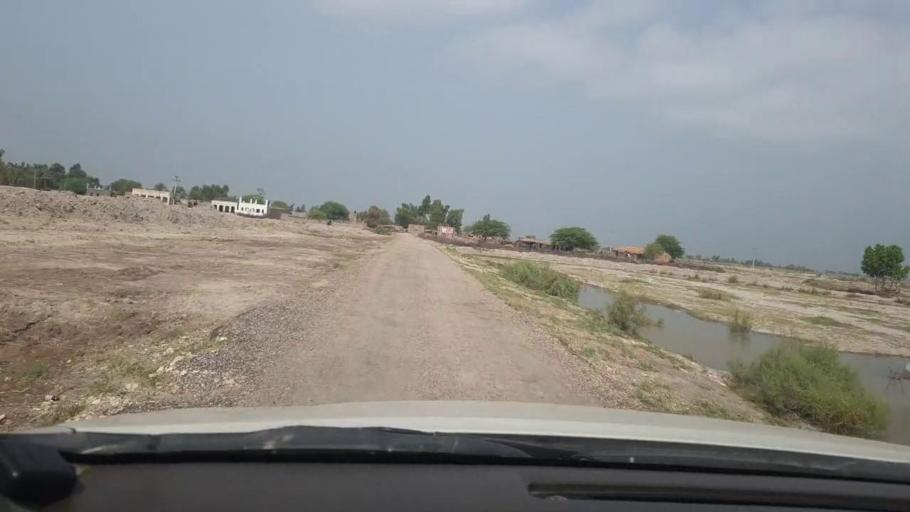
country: PK
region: Sindh
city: Shikarpur
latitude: 28.0252
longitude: 68.5860
